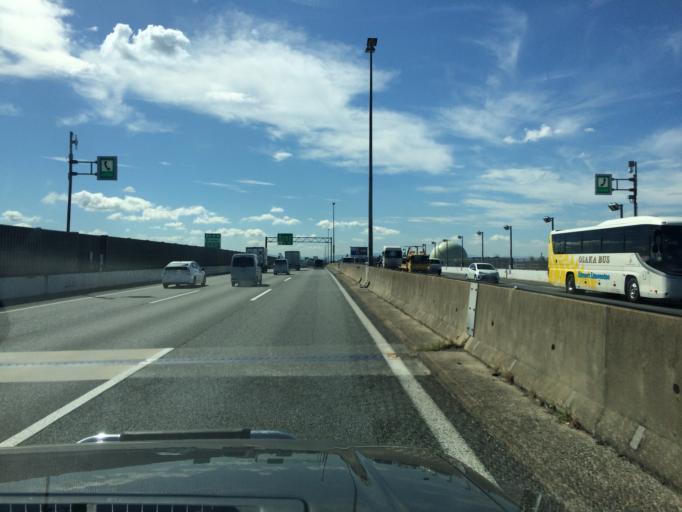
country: JP
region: Osaka
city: Daitocho
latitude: 34.7015
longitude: 135.5921
